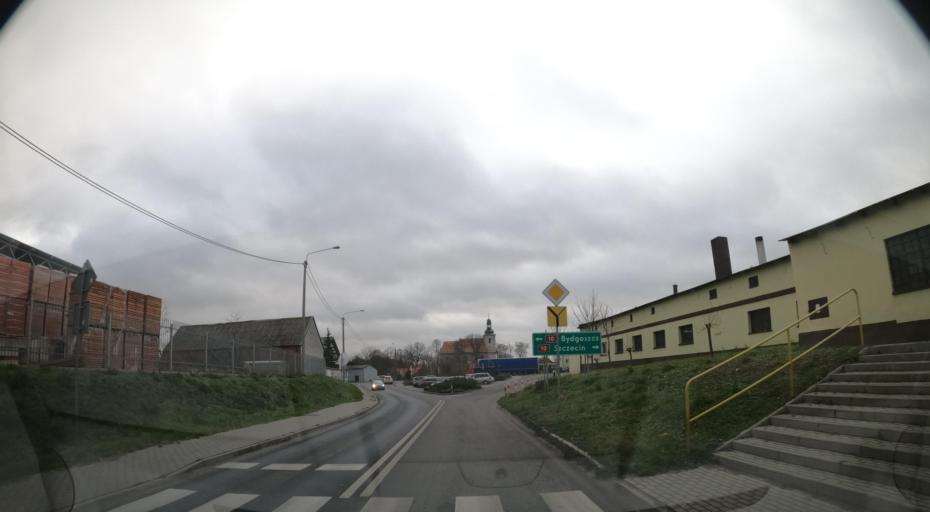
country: PL
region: Kujawsko-Pomorskie
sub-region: Powiat nakielski
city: Sadki
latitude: 53.1610
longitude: 17.4480
